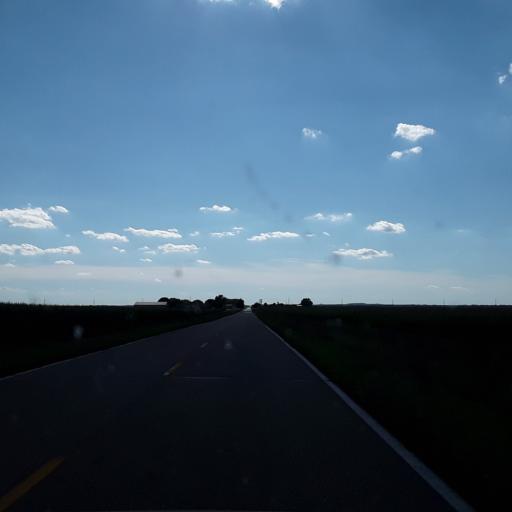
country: US
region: Nebraska
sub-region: Hall County
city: Wood River
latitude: 40.8879
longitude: -98.6205
